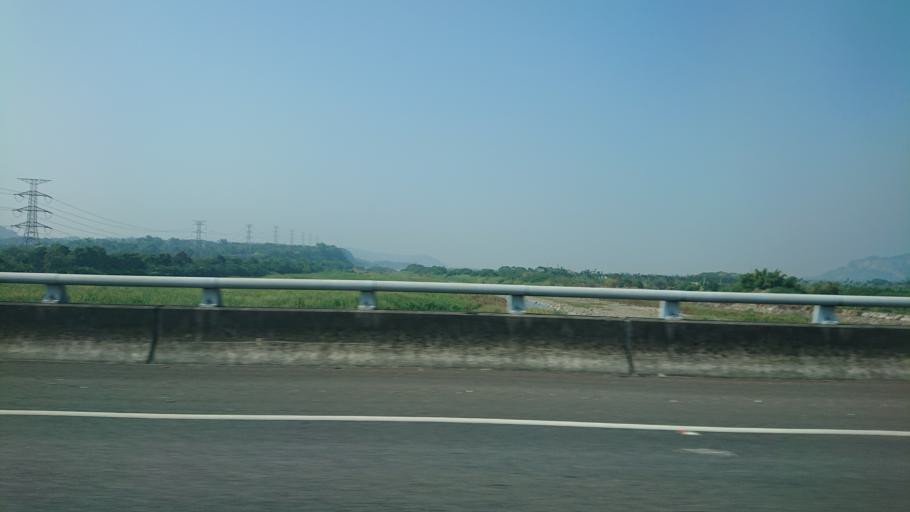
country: TW
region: Taiwan
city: Lugu
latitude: 23.7913
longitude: 120.7037
